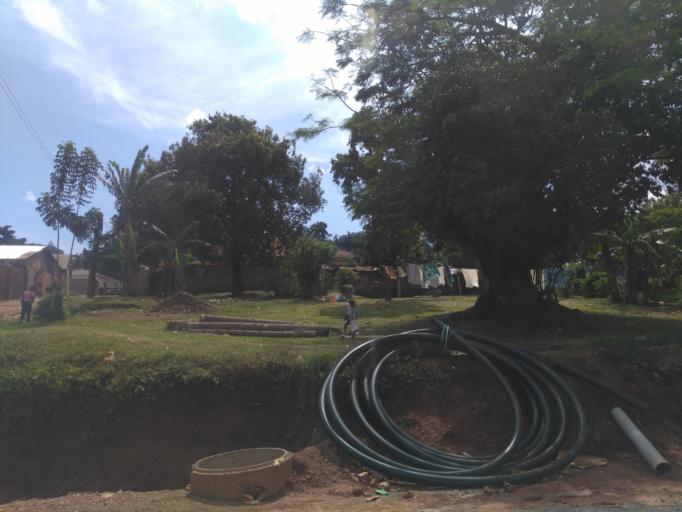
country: UG
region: Central Region
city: Kampala Central Division
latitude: 0.3447
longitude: 32.5656
